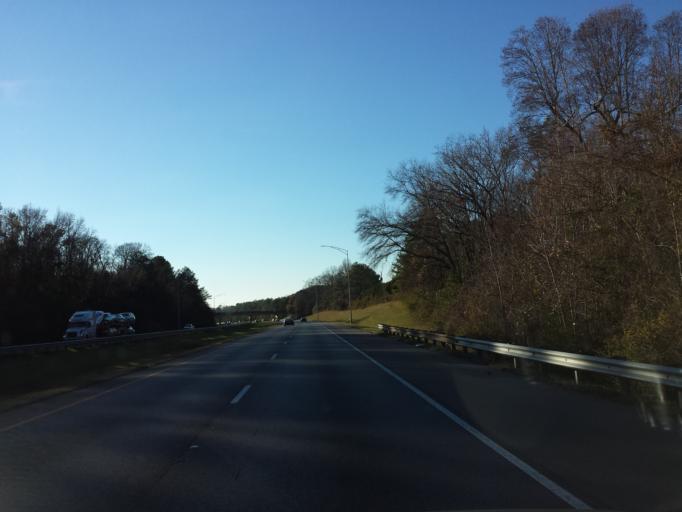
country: US
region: Alabama
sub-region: Tuscaloosa County
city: Holt
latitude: 33.1762
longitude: -87.4980
